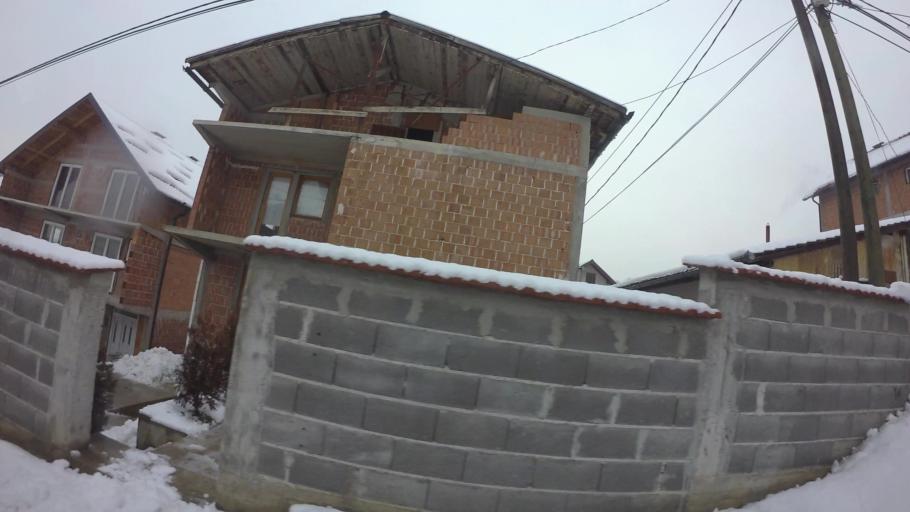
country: BA
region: Federation of Bosnia and Herzegovina
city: Vogosca
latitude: 43.8788
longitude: 18.3217
